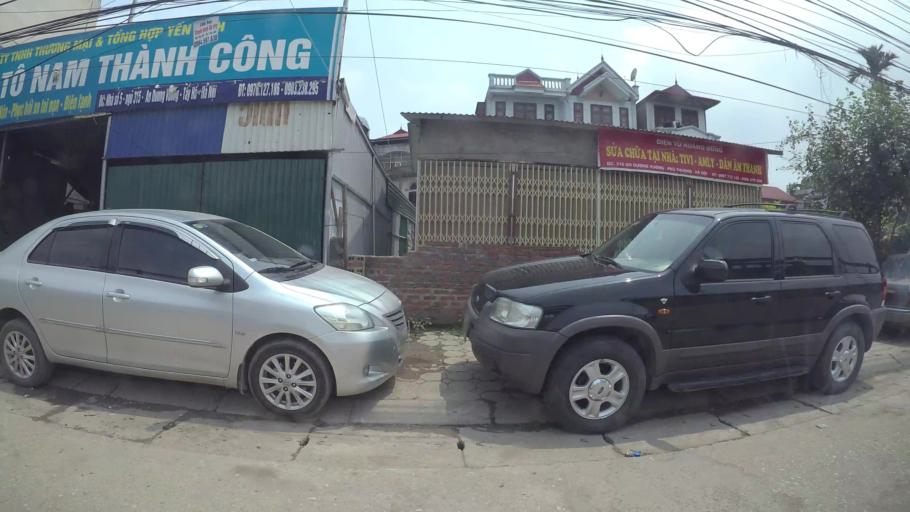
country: VN
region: Ha Noi
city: Tay Ho
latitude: 21.0896
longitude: 105.8037
